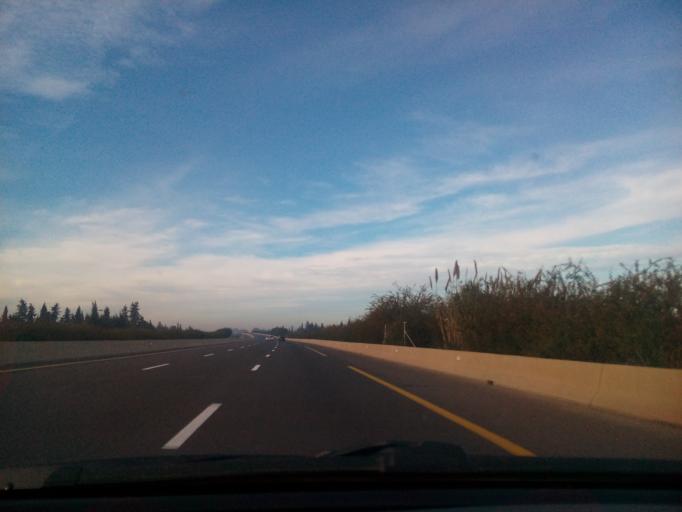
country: DZ
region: Mascara
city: Mascara
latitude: 35.6220
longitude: 0.0541
